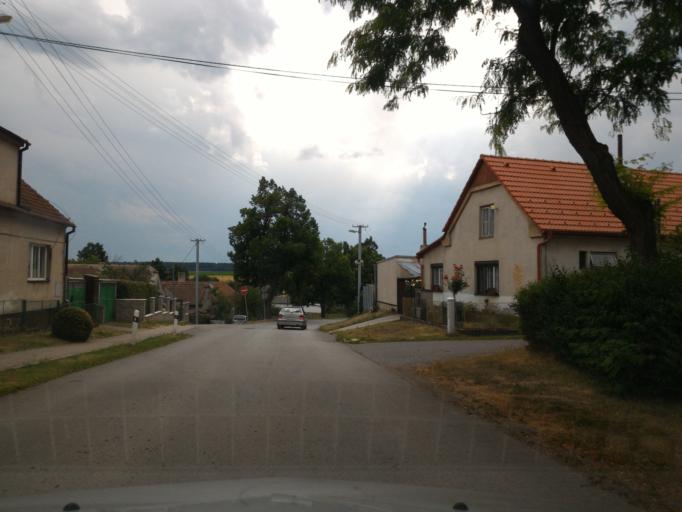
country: CZ
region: Vysocina
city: Moravske Budejovice
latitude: 49.0671
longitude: 15.7653
